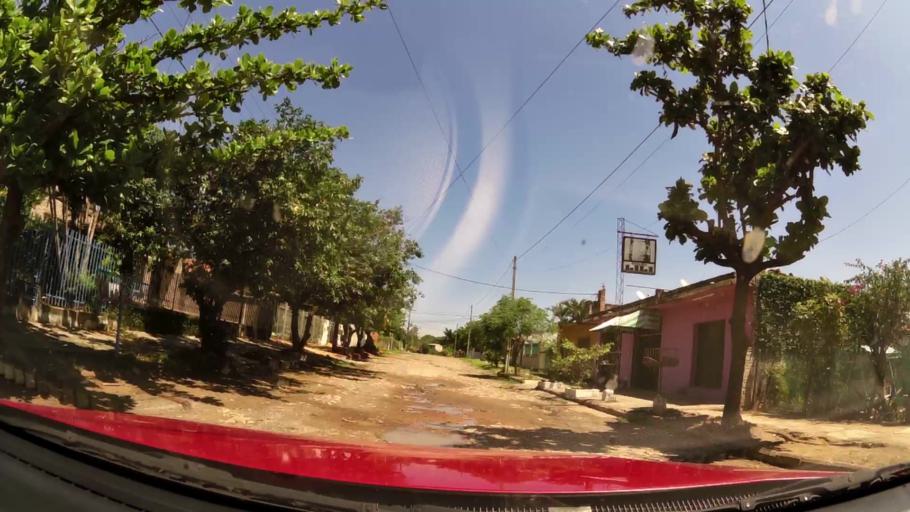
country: PY
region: Central
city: Colonia Mariano Roque Alonso
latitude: -25.2357
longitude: -57.5464
